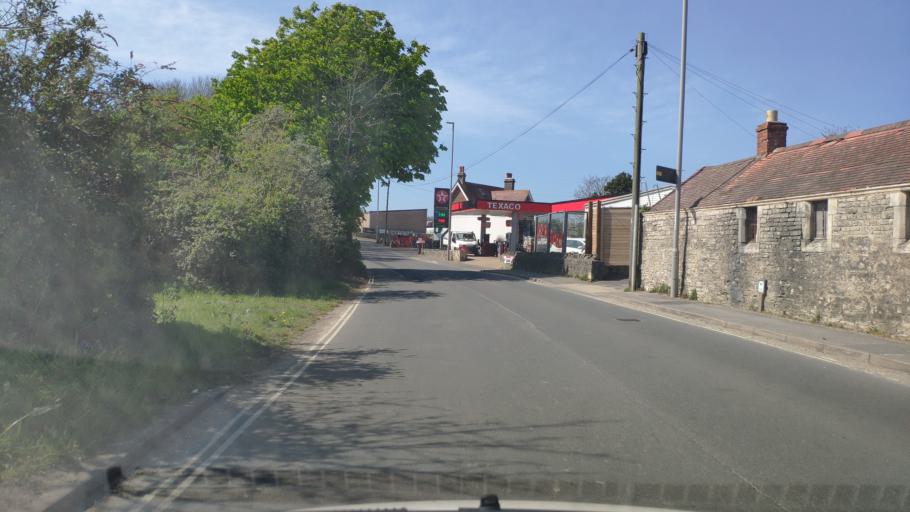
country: GB
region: England
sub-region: Dorset
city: Swanage
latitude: 50.6132
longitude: -1.9715
